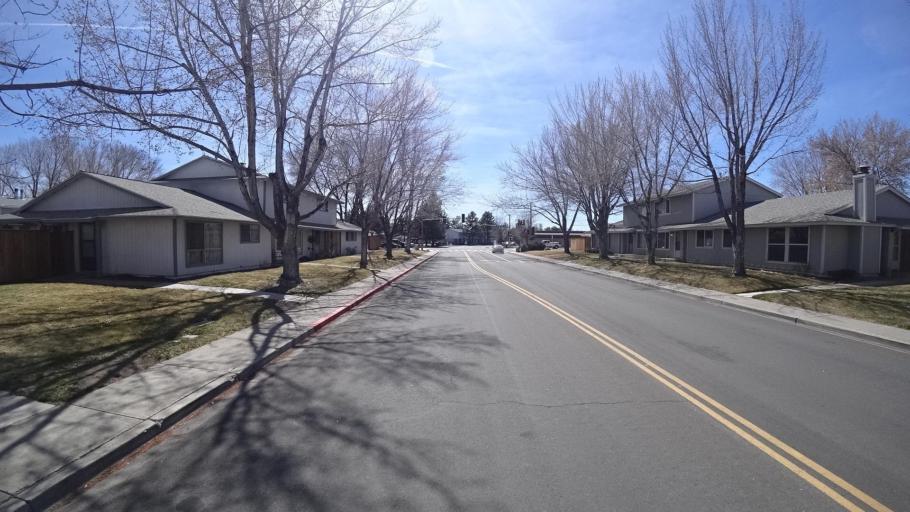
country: US
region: Nevada
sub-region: Washoe County
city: Sparks
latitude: 39.5426
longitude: -119.7306
